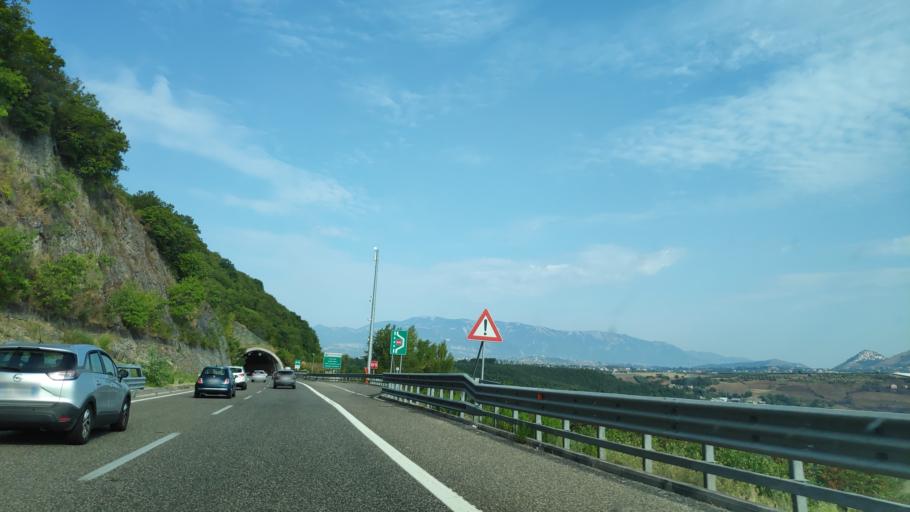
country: IT
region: Campania
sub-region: Provincia di Salerno
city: Sicignano degli Alburni
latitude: 40.5995
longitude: 15.3125
